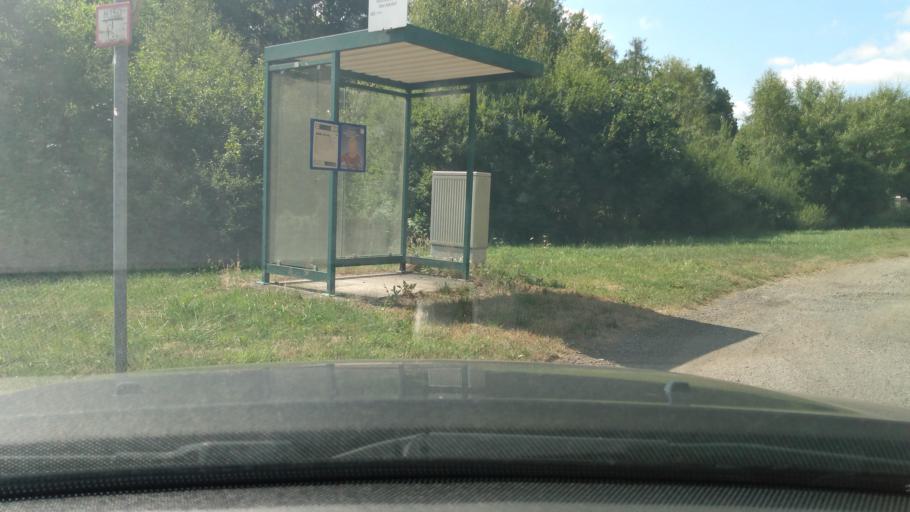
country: DE
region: Rheinland-Pfalz
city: Horbruch
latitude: 49.9061
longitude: 7.2262
